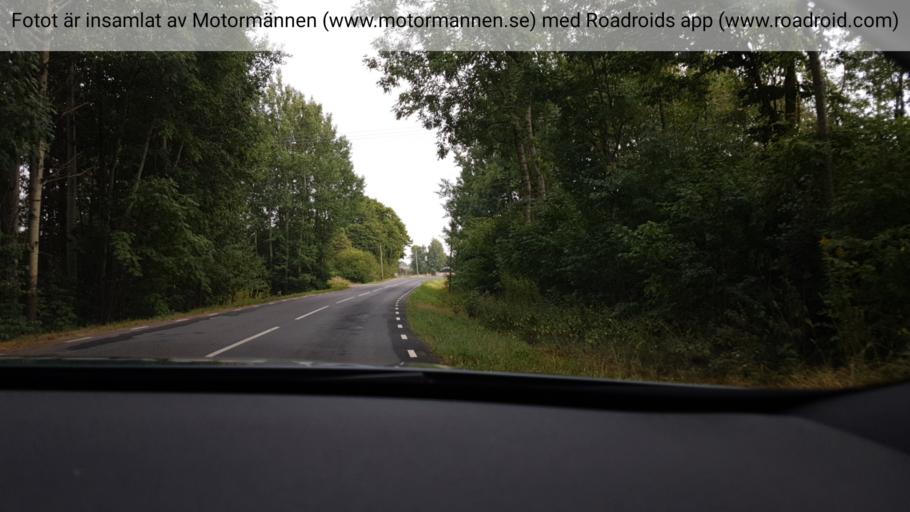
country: SE
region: Vaestra Goetaland
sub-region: Falkopings Kommun
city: Akarp
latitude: 58.1890
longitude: 13.6272
